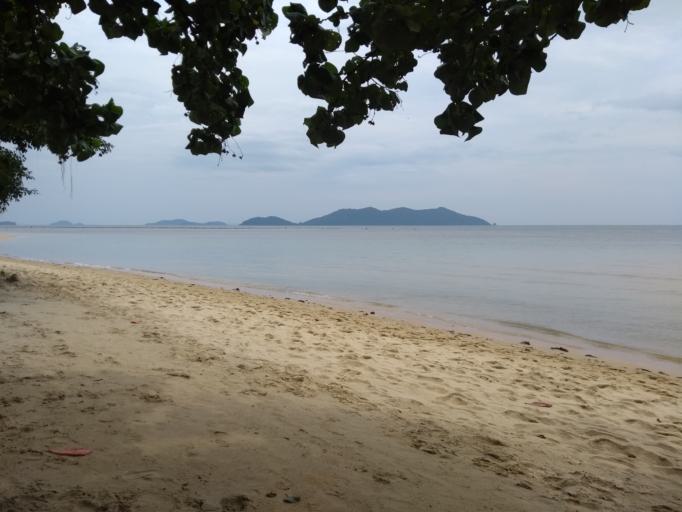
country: TH
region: Trat
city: Ko Chang Tai
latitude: 11.9744
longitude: 102.3241
